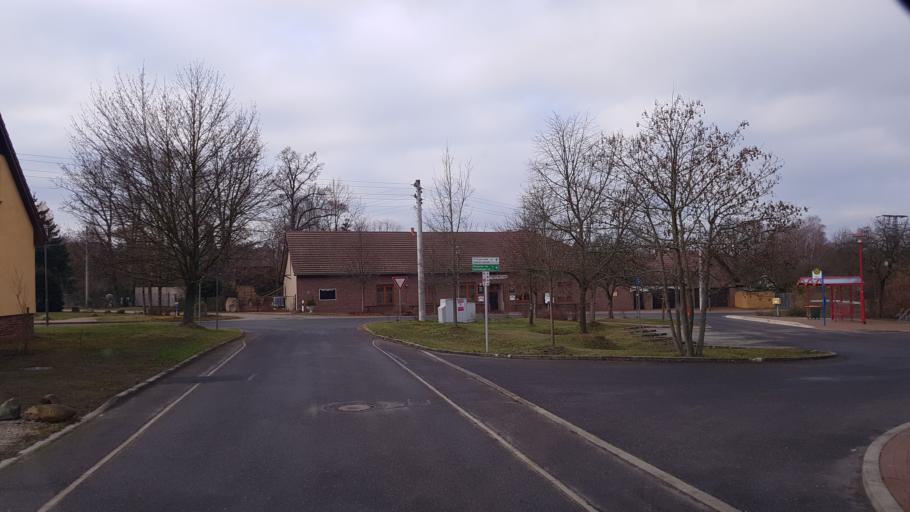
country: DE
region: Brandenburg
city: Sallgast
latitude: 51.5877
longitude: 13.8168
